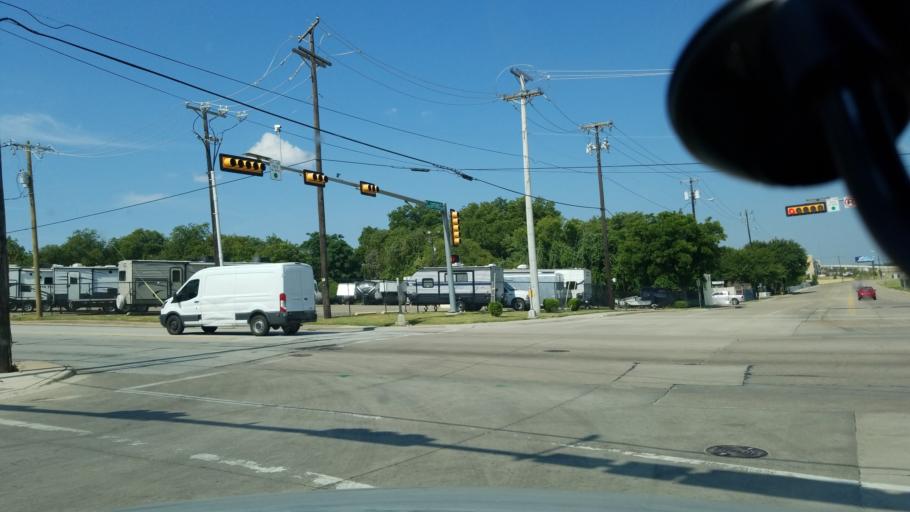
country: US
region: Texas
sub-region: Dallas County
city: Grand Prairie
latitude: 32.7603
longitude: -96.9598
